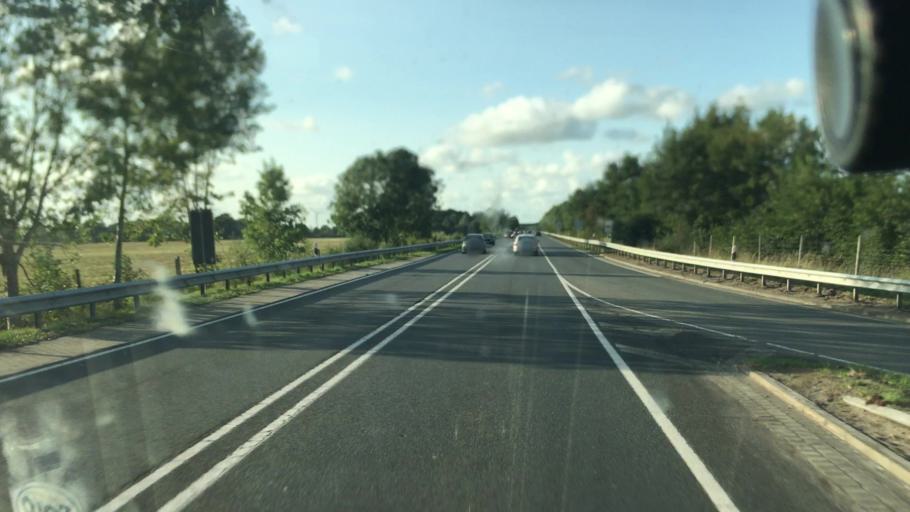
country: DE
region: Lower Saxony
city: Schortens
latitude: 53.5644
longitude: 7.9391
